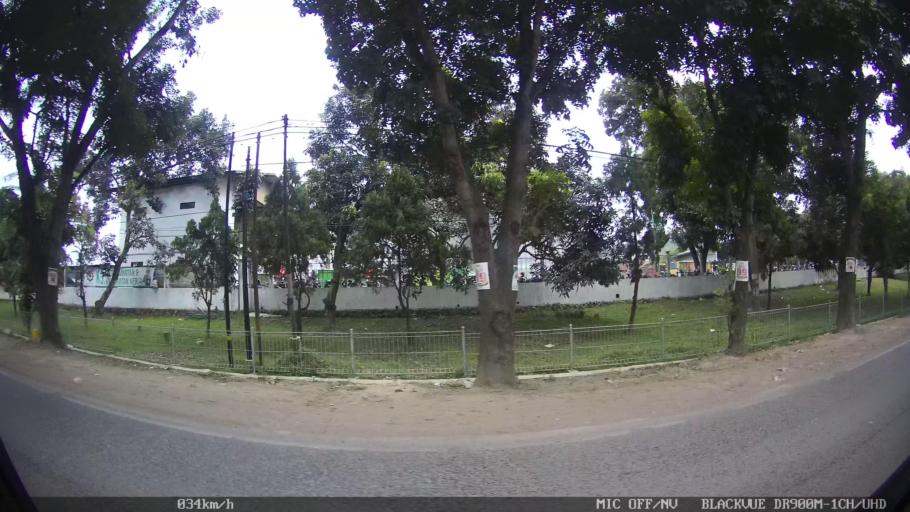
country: ID
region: Lampung
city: Panjang
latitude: -5.4206
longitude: 105.3345
